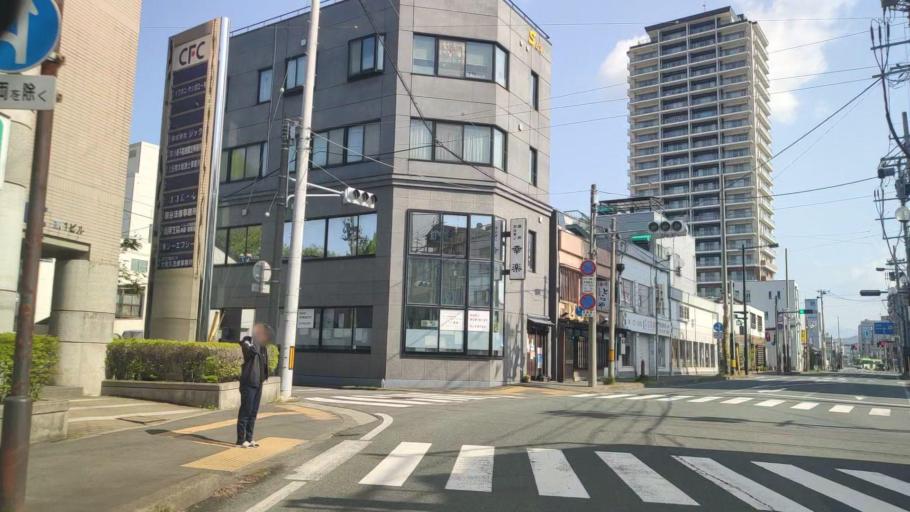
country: JP
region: Iwate
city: Morioka-shi
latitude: 39.6978
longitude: 141.1565
